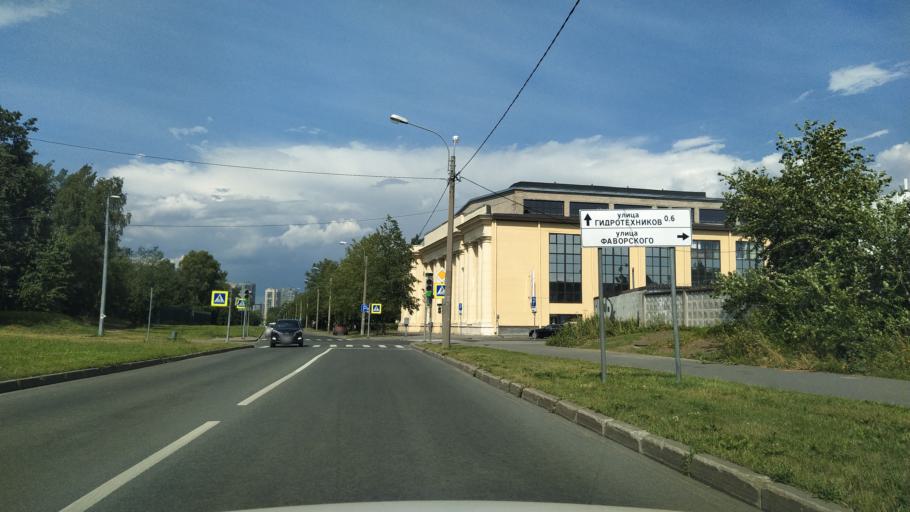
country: RU
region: Leningrad
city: Kalininskiy
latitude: 60.0019
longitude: 30.3816
